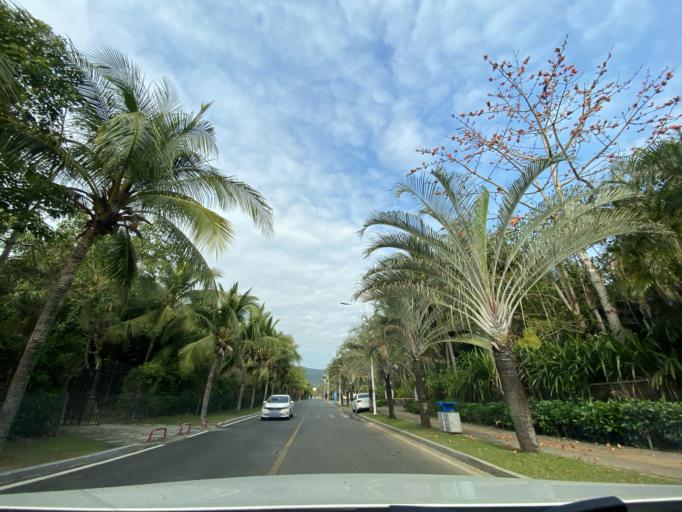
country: CN
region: Hainan
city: Tiandu
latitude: 18.2280
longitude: 109.6225
